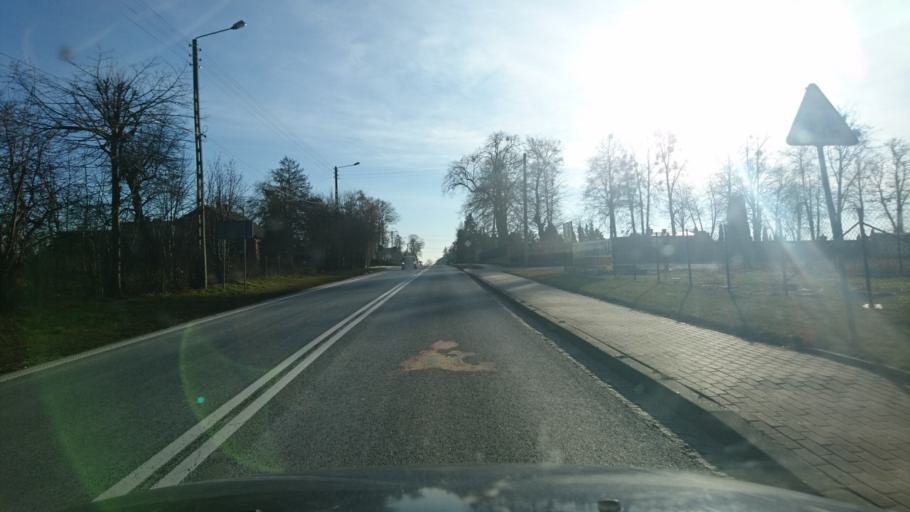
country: PL
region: Opole Voivodeship
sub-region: Powiat oleski
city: Dalachow
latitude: 51.0427
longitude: 18.5969
